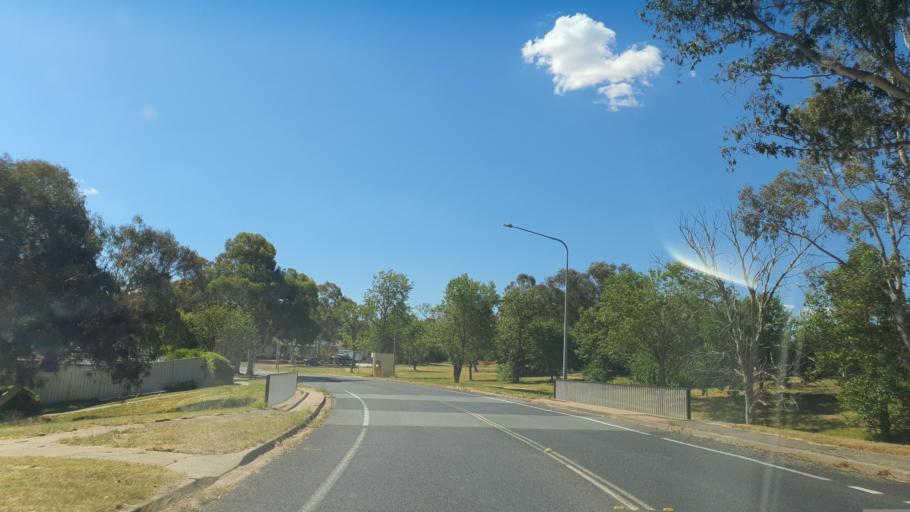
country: AU
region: Australian Capital Territory
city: Belconnen
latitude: -35.2089
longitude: 149.0426
